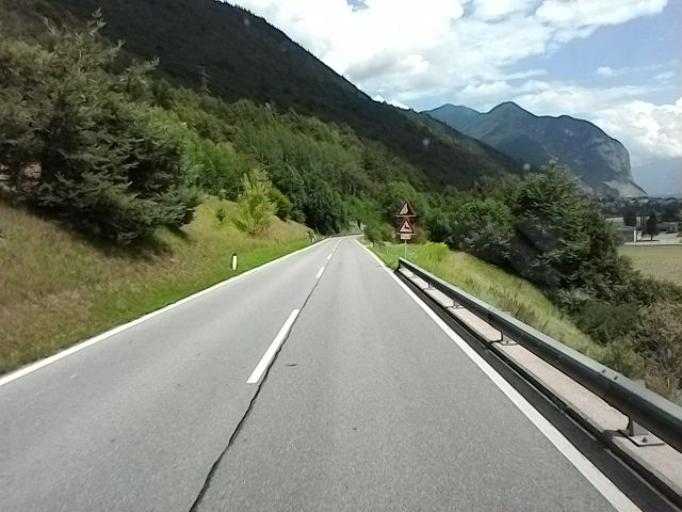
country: AT
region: Tyrol
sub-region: Politischer Bezirk Innsbruck Land
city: Ranggen
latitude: 47.2802
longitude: 11.2108
